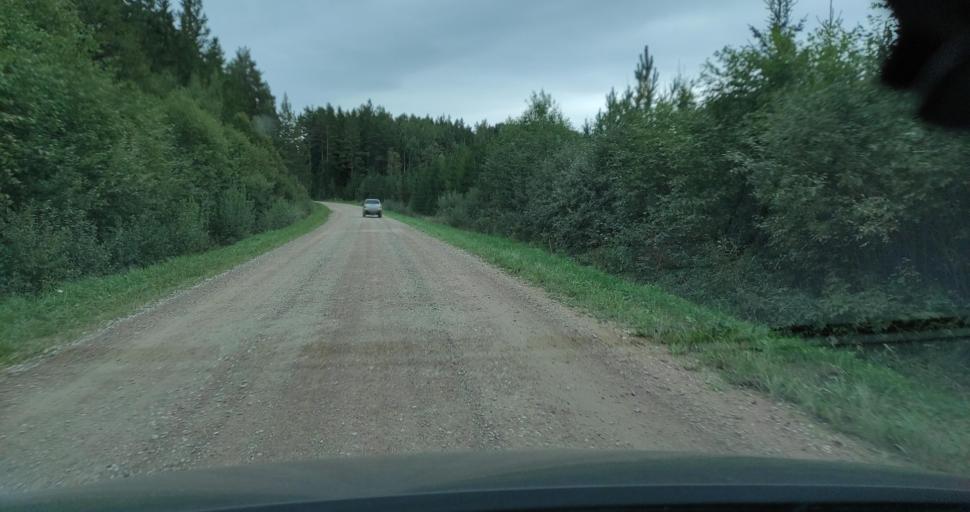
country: LV
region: Talsu Rajons
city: Stende
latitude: 57.0383
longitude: 22.3128
